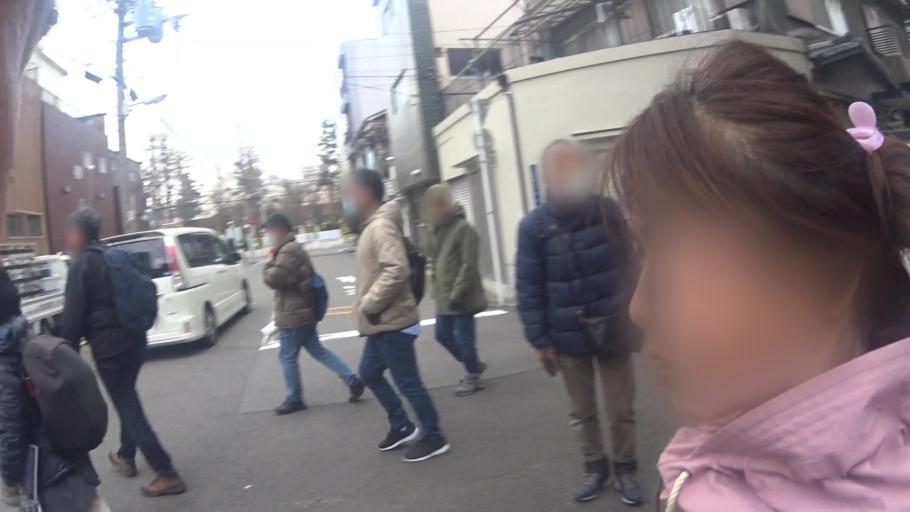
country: JP
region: Osaka
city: Osaka-shi
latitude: 34.6770
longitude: 135.5295
